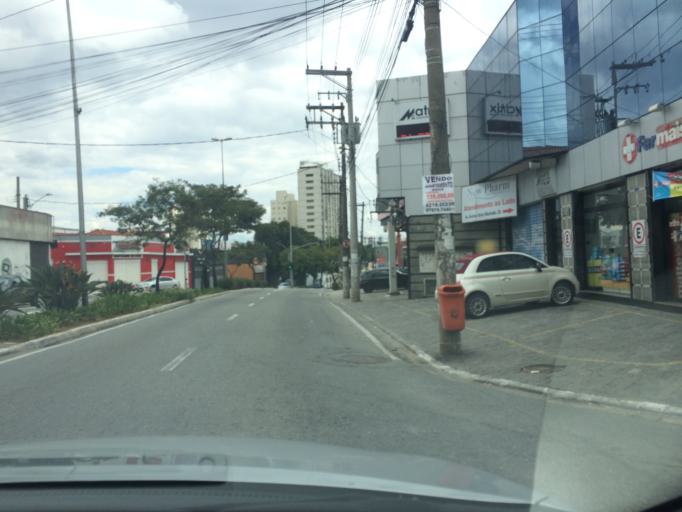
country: BR
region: Sao Paulo
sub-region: Guarulhos
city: Guarulhos
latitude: -23.4613
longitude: -46.5240
